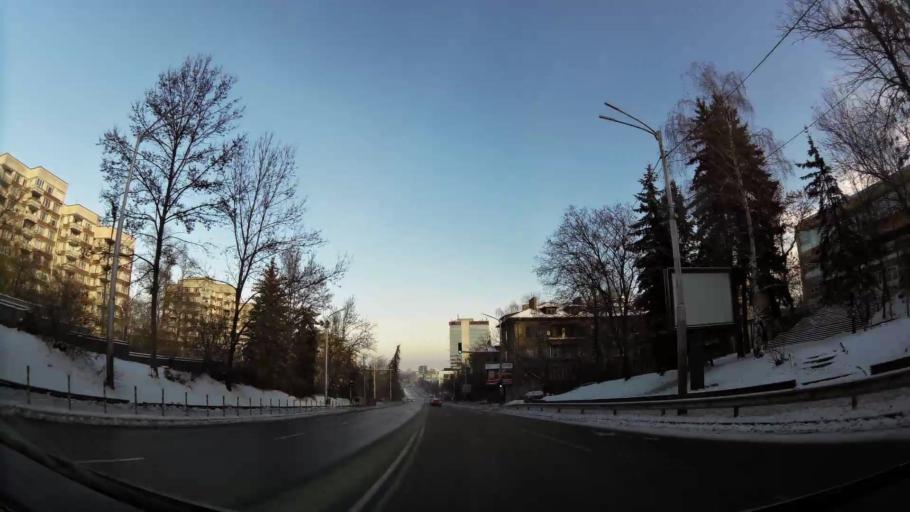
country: BG
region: Sofia-Capital
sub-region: Stolichna Obshtina
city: Sofia
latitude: 42.6747
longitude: 23.3221
